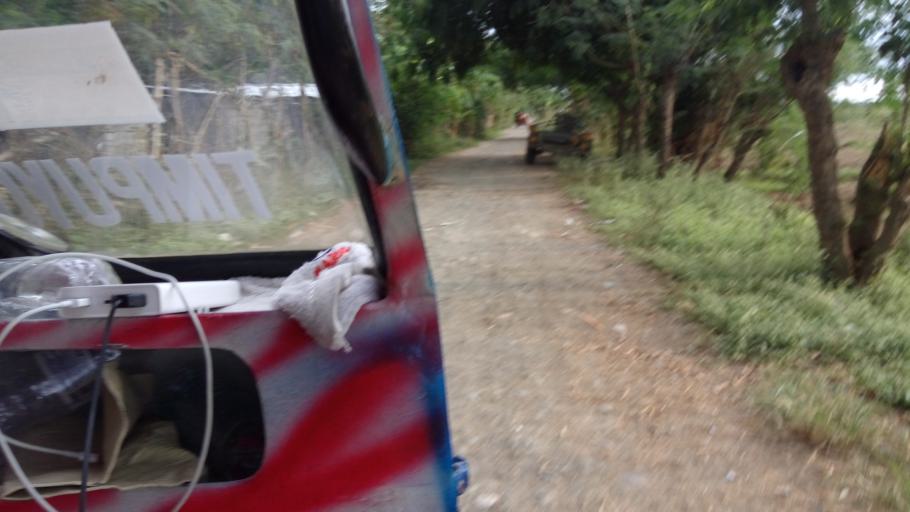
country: PH
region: Ilocos
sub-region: Province of La Union
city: Santo Tomas
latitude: 16.2796
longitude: 120.3861
